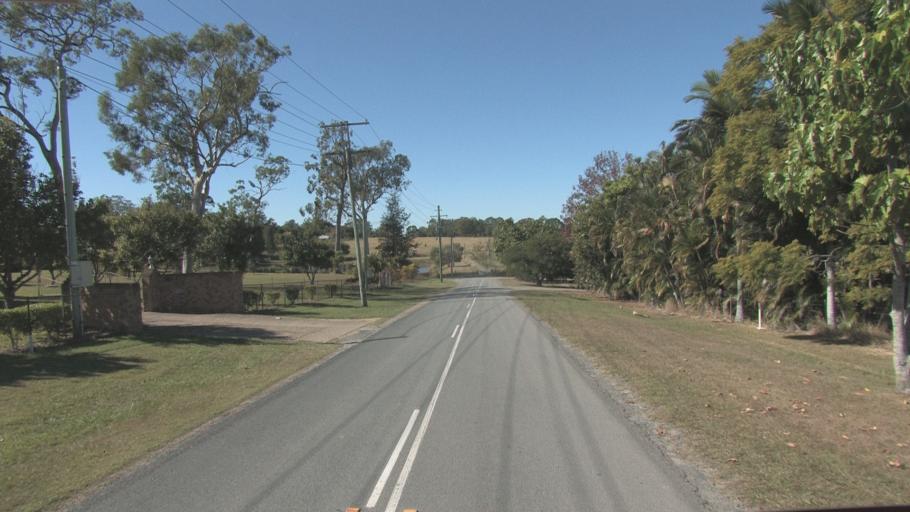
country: AU
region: Queensland
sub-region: Logan
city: Park Ridge South
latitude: -27.7080
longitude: 153.0527
